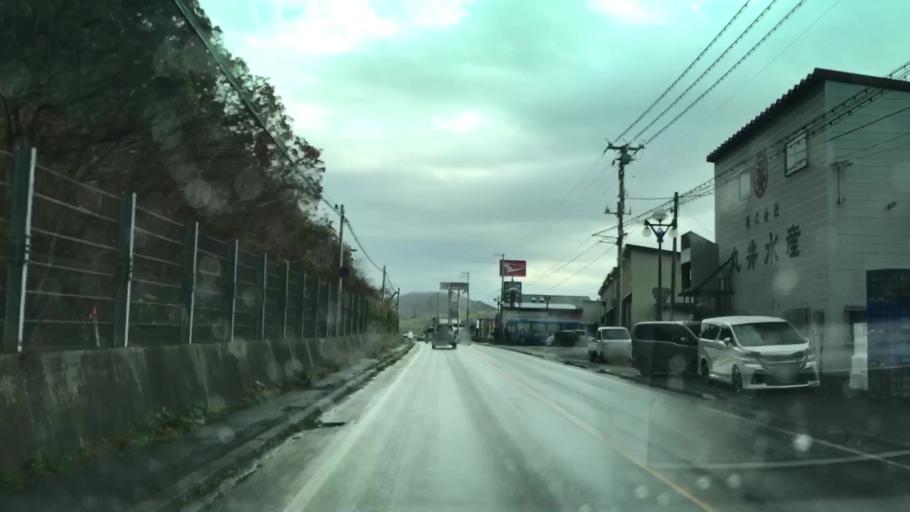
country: JP
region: Hokkaido
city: Shizunai-furukawacho
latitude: 42.1769
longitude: 142.7525
